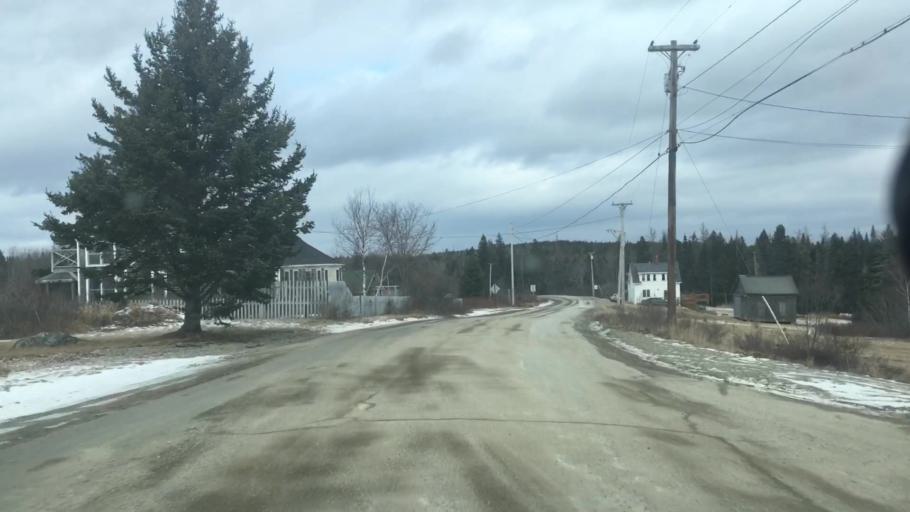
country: US
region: Maine
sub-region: Washington County
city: Machias
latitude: 44.6134
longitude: -67.4801
